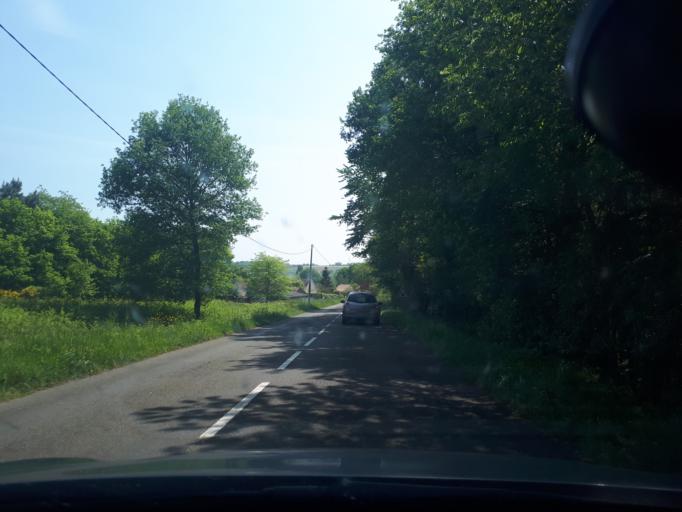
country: FR
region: Pays de la Loire
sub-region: Departement de la Sarthe
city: Le Breil-sur-Merize
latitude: 48.0203
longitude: 0.4546
